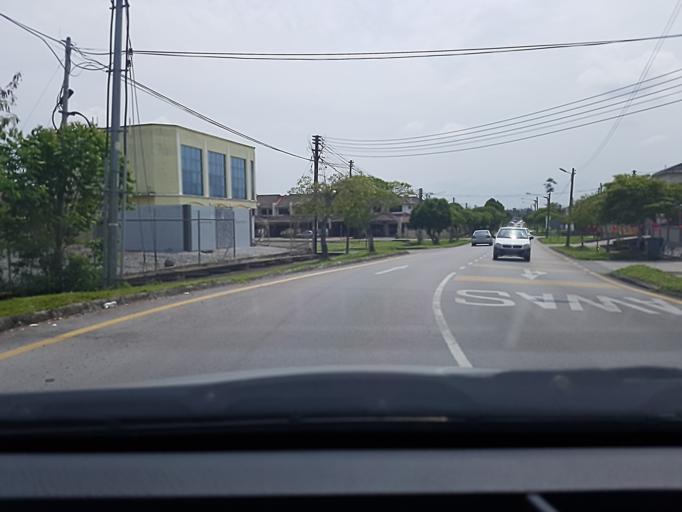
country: MY
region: Sarawak
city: Kuching
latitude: 1.5128
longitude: 110.3619
